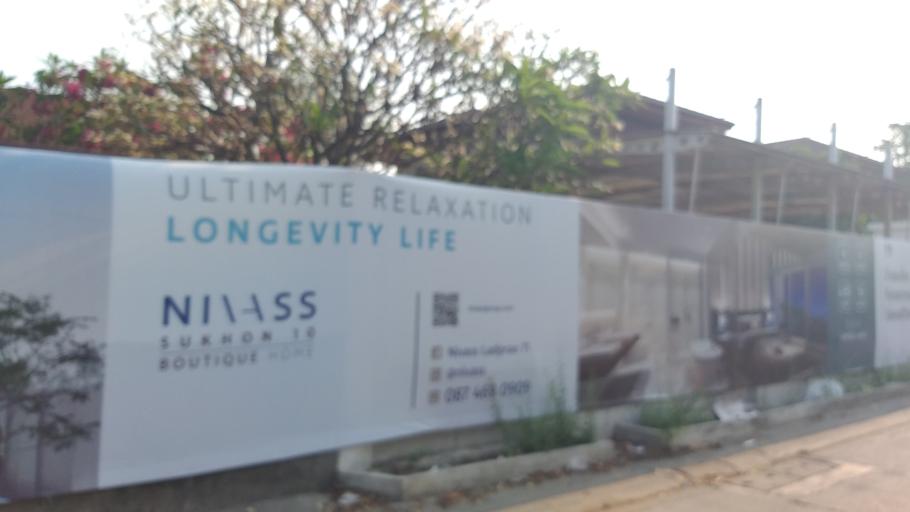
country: TH
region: Bangkok
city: Lat Phrao
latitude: 13.8223
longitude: 100.6133
